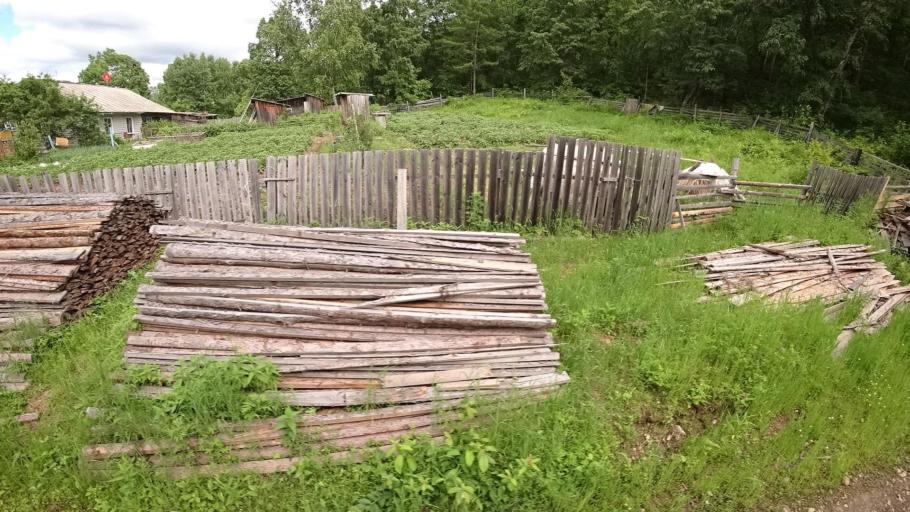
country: RU
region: Khabarovsk Krai
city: Litovko
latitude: 49.3626
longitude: 135.1745
